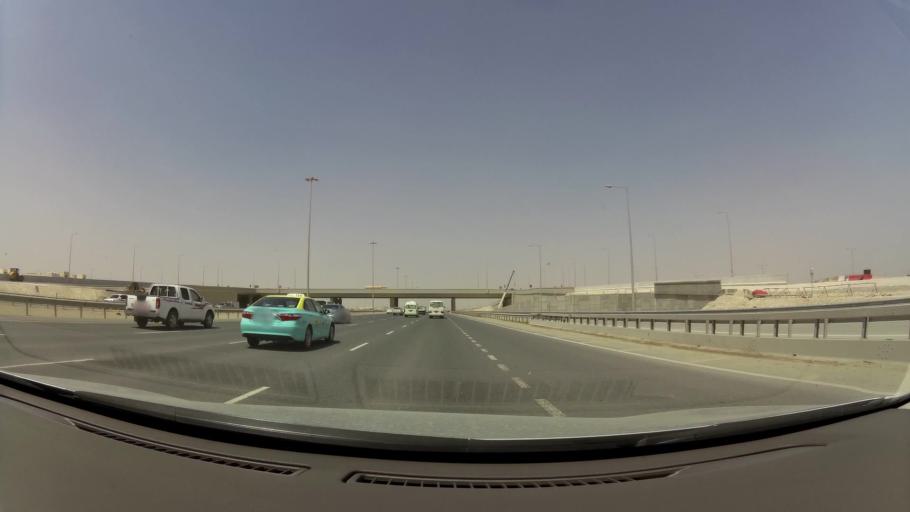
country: QA
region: Baladiyat Umm Salal
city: Umm Salal Muhammad
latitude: 25.4095
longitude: 51.4255
